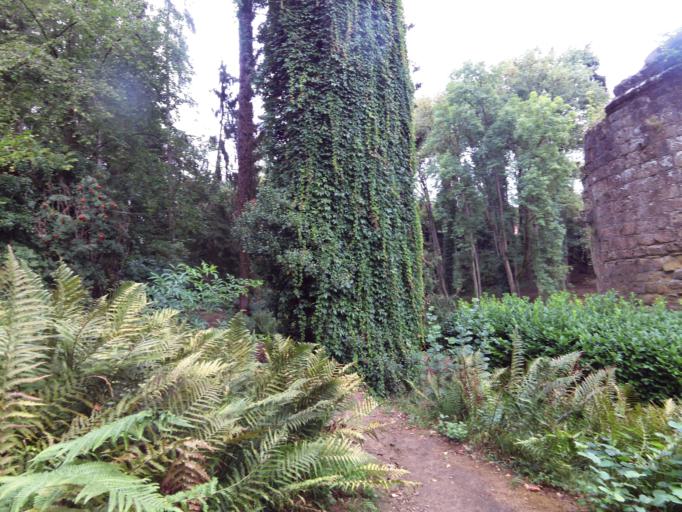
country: LU
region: Grevenmacher
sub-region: Canton d'Echternach
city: Beaufort
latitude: 49.8339
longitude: 6.2869
